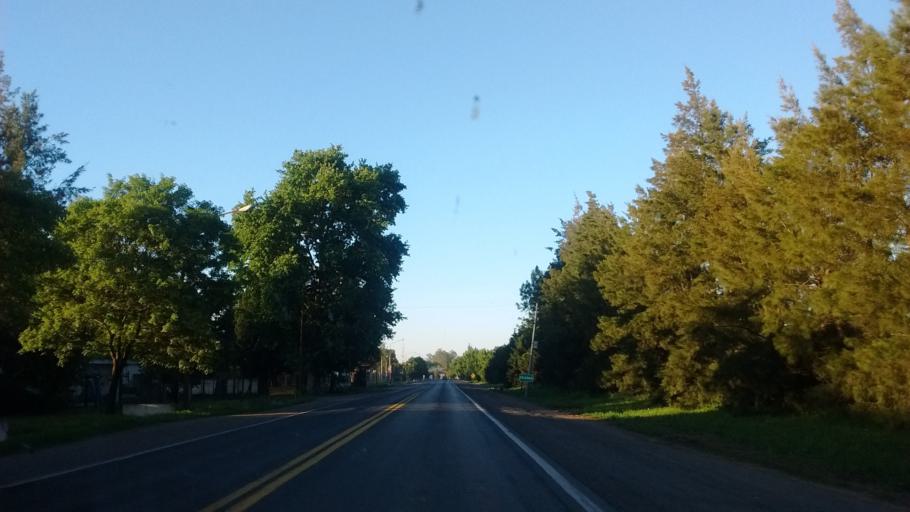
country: AR
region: Santa Fe
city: Firmat
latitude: -33.2346
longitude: -61.3512
